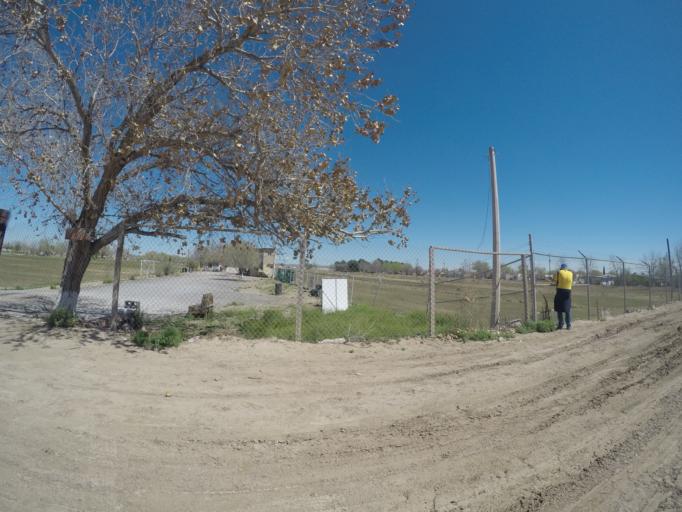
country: US
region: Texas
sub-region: El Paso County
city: Socorro Mission Number 1 Colonia
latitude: 31.6091
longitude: -106.3131
